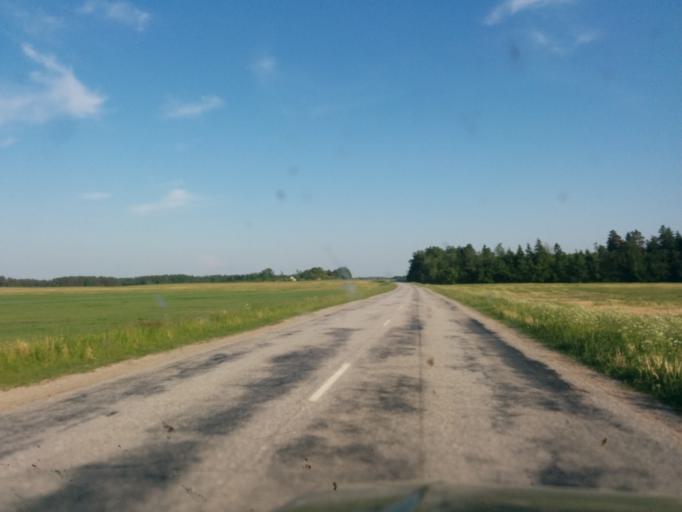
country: LV
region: Talsu Rajons
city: Talsi
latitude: 57.3119
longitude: 22.5382
